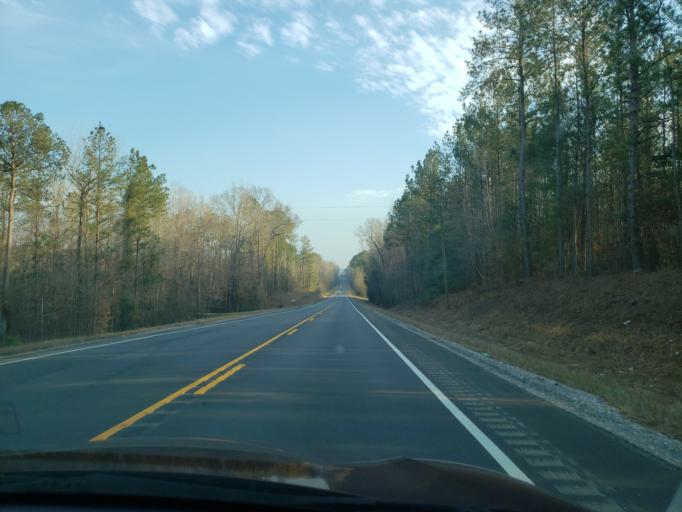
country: US
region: Alabama
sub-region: Hale County
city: Greensboro
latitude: 32.8506
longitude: -87.6117
